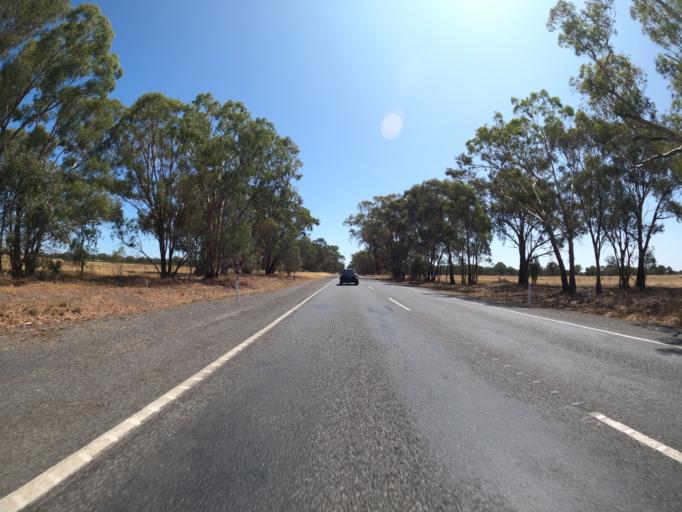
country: AU
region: New South Wales
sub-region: Corowa Shire
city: Corowa
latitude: -36.0605
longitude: 146.4146
